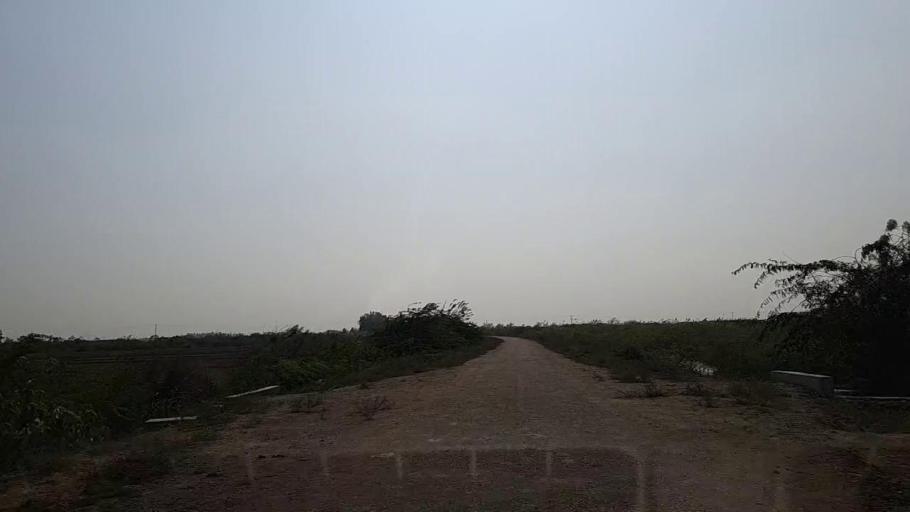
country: PK
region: Sindh
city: Mirpur Sakro
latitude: 24.6533
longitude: 67.6908
